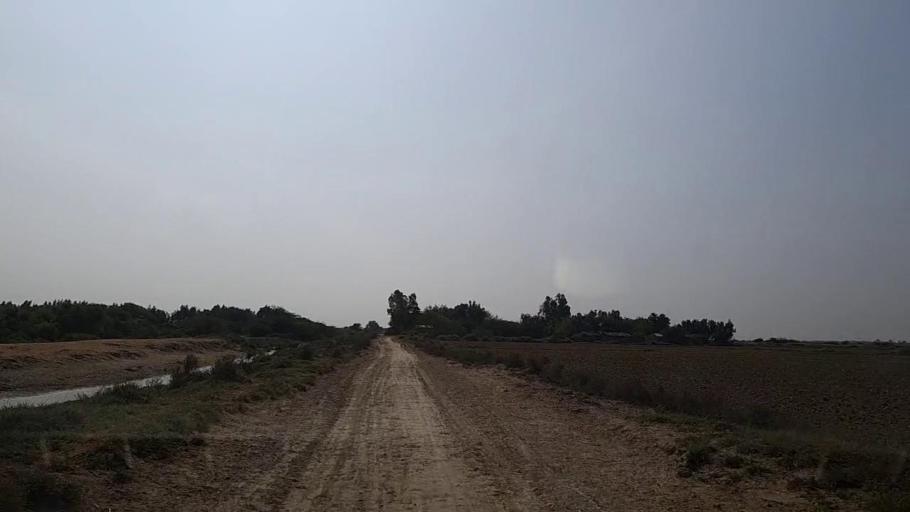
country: PK
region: Sindh
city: Mirpur Sakro
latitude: 24.5488
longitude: 67.7908
